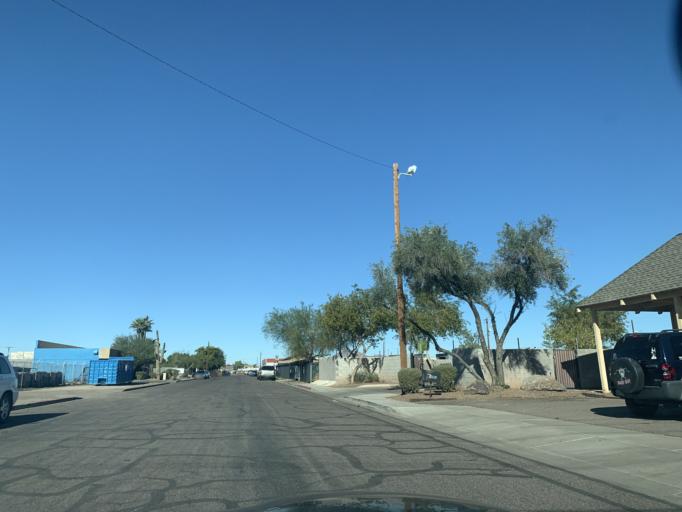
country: US
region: Arizona
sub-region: Maricopa County
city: Tempe Junction
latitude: 33.4184
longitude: -111.9852
